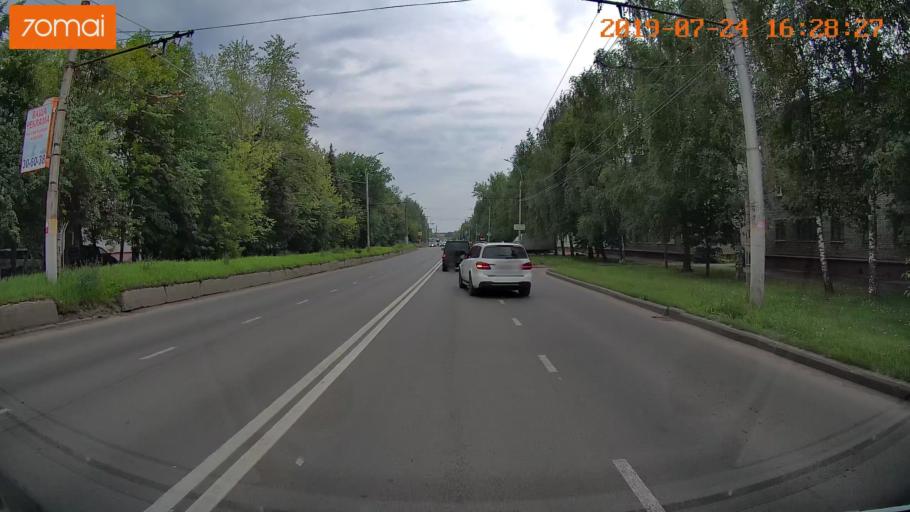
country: RU
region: Ivanovo
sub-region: Gorod Ivanovo
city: Ivanovo
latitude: 56.9711
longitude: 40.9640
